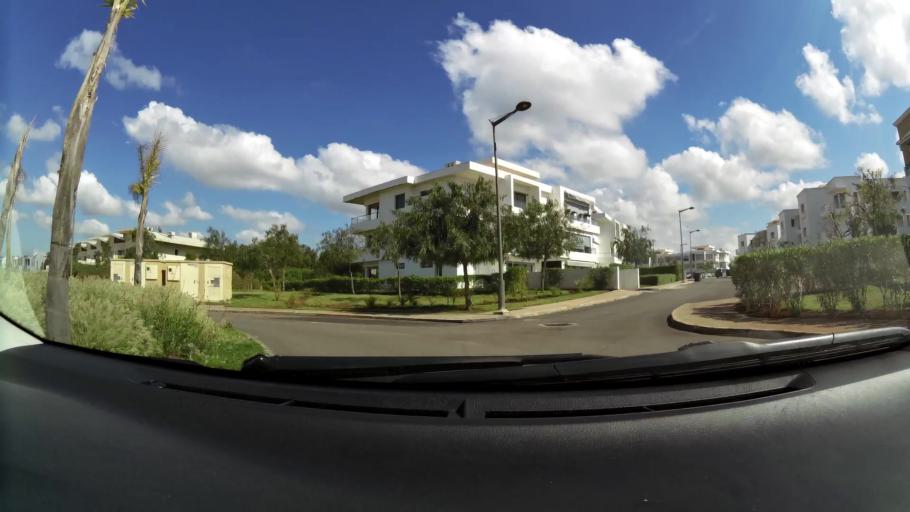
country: MA
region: Grand Casablanca
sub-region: Nouaceur
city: Bouskoura
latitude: 33.4716
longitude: -7.6033
